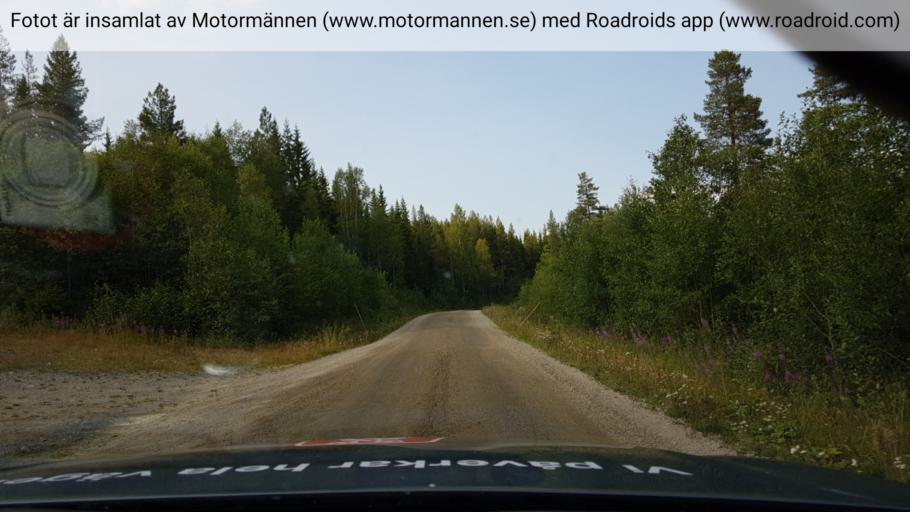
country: SE
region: Jaemtland
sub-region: OEstersunds Kommun
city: Brunflo
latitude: 62.5831
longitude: 14.9033
